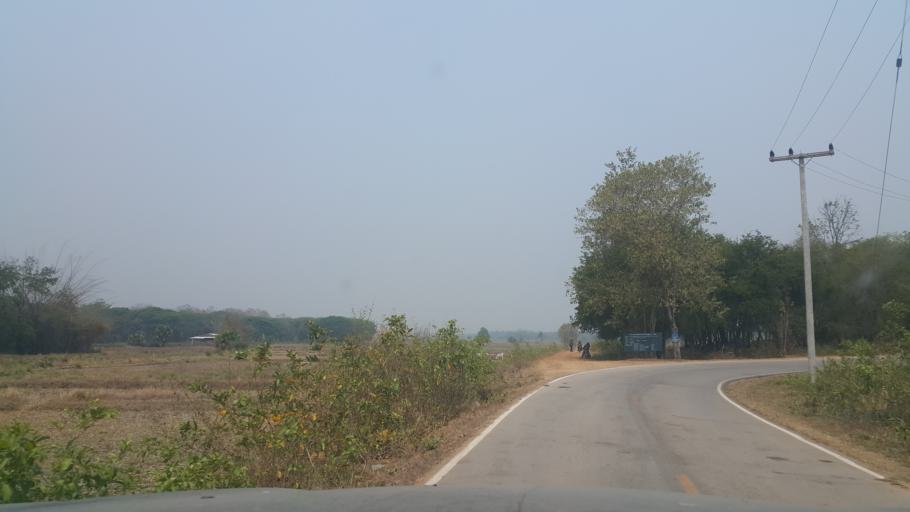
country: TH
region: Lampang
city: Sop Prap
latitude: 17.8946
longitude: 99.3146
